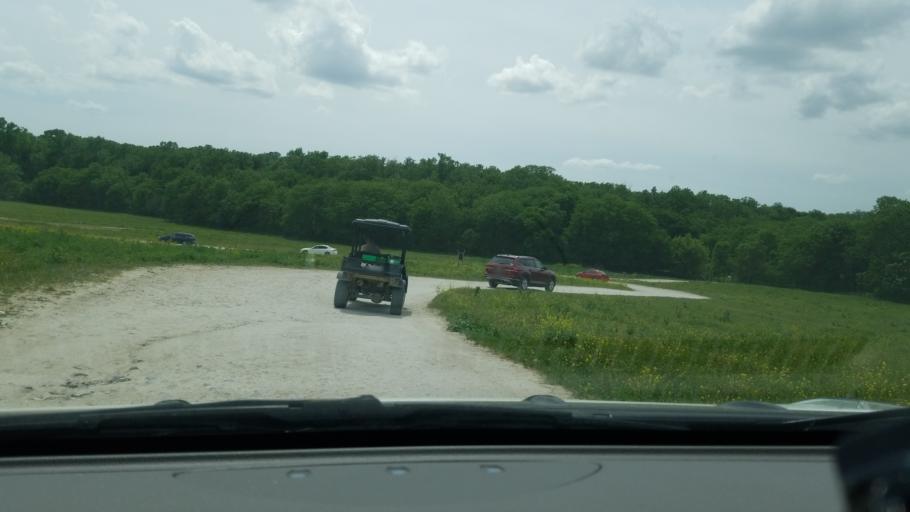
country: US
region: Nebraska
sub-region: Saunders County
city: Ashland
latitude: 41.0185
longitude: -96.2941
